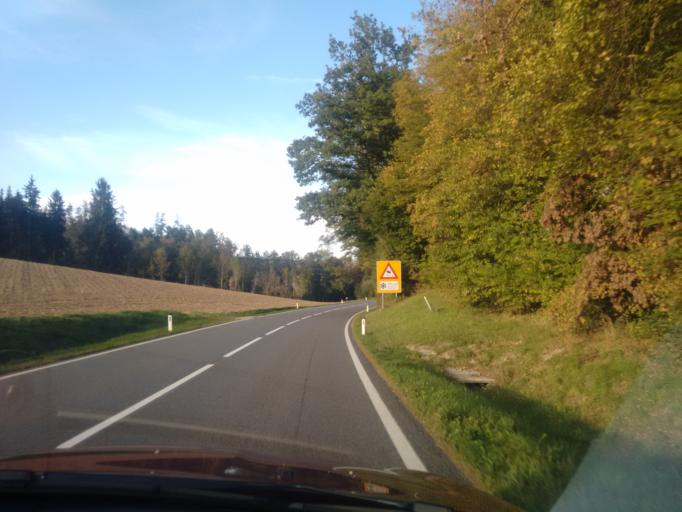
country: AT
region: Upper Austria
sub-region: Politischer Bezirk Vocklabruck
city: Niederthalheim
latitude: 48.1543
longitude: 13.7347
